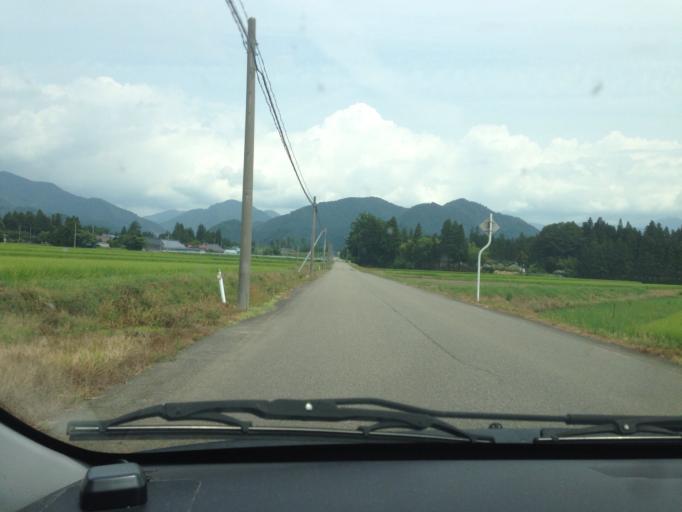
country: JP
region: Fukushima
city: Kitakata
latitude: 37.7156
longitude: 139.8604
